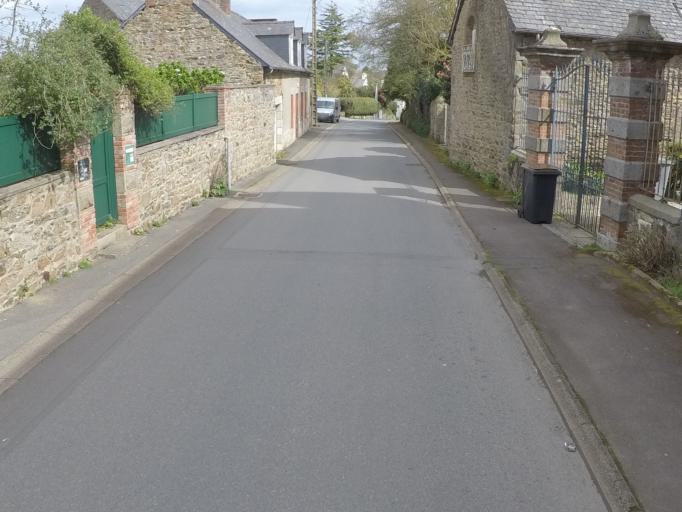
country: FR
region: Brittany
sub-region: Departement des Cotes-d'Armor
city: Plouha
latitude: 48.6760
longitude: -2.9261
